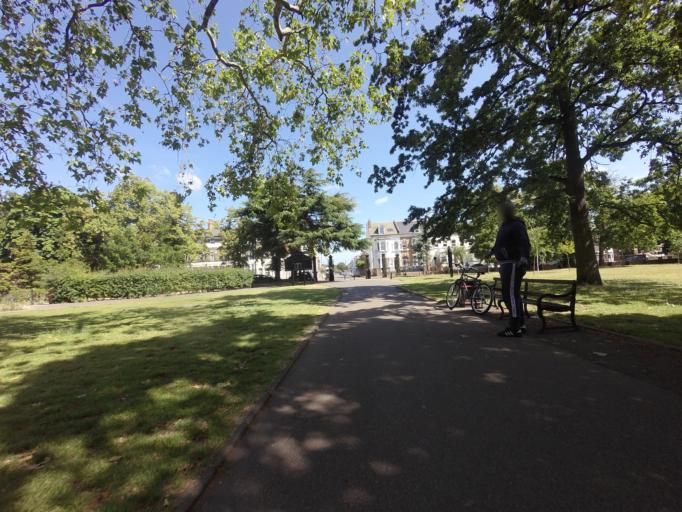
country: GB
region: England
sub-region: Greater London
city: East Ham
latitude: 51.5410
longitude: 0.0199
